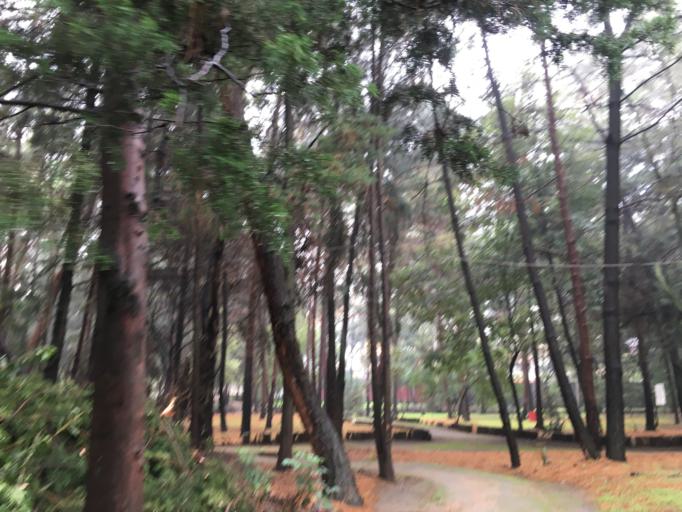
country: MX
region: Mexico City
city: Tlalpan
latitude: 19.2823
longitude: -99.1470
